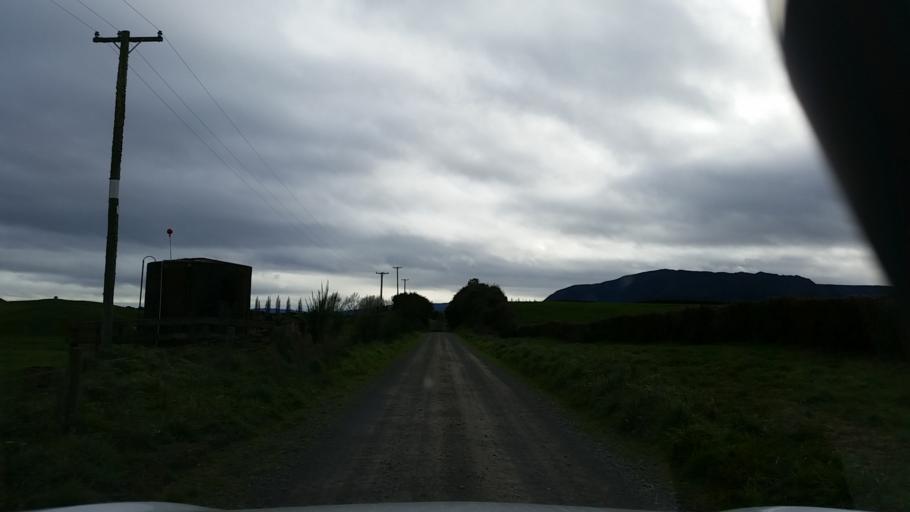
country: NZ
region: Bay of Plenty
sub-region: Whakatane District
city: Murupara
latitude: -38.3093
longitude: 176.4689
